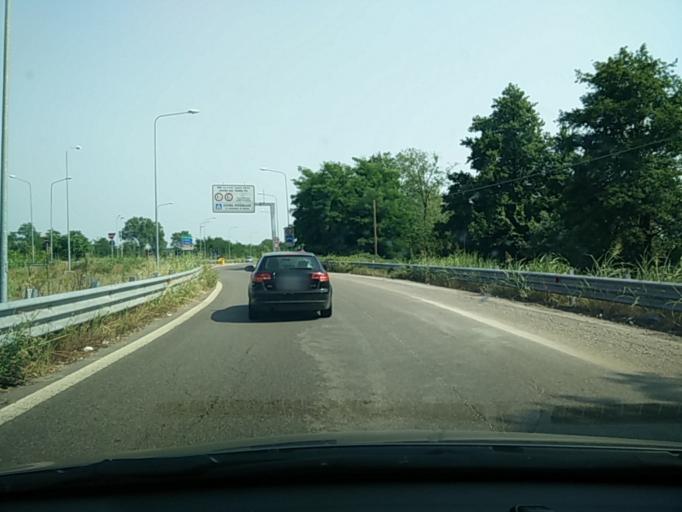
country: IT
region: Lombardy
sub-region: Provincia di Pavia
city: Valle Salimbene
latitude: 45.1653
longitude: 9.2143
